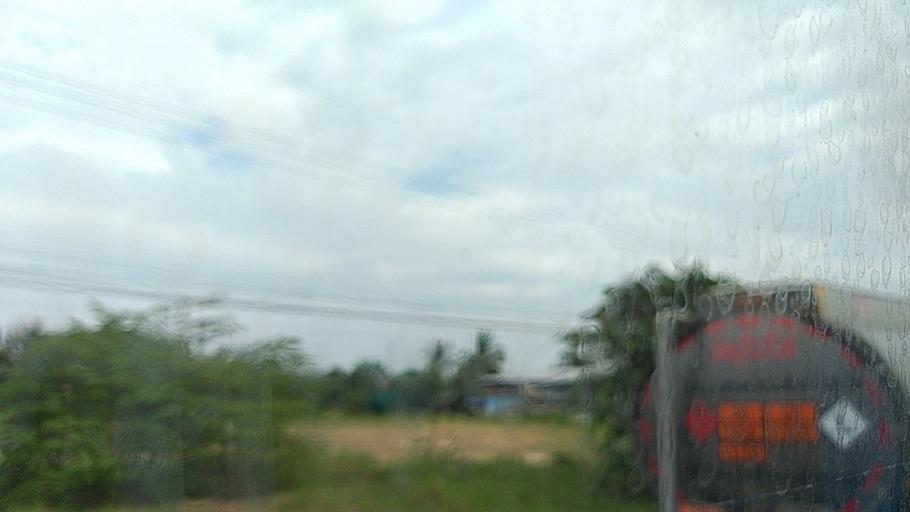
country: TH
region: Roi Et
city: Changhan
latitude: 16.1229
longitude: 103.4805
